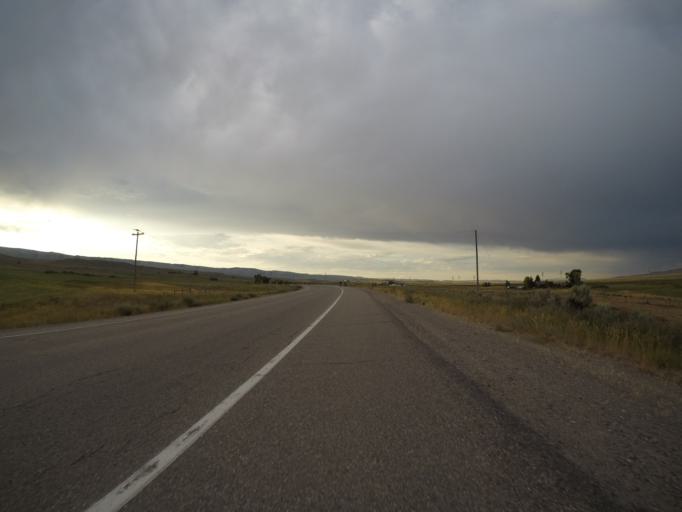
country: US
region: Idaho
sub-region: Bear Lake County
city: Montpelier
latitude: 42.0713
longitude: -110.9445
